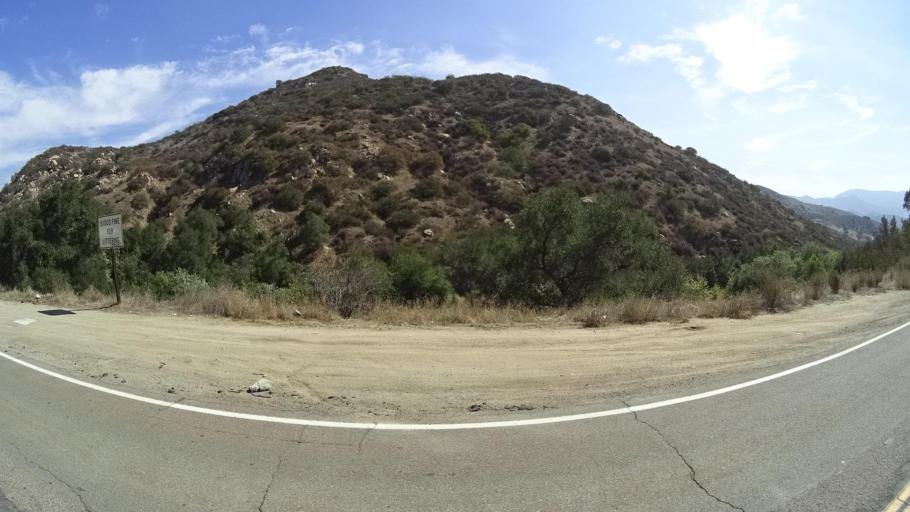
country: US
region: California
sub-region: San Diego County
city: Harbison Canyon
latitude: 32.8107
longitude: -116.8433
